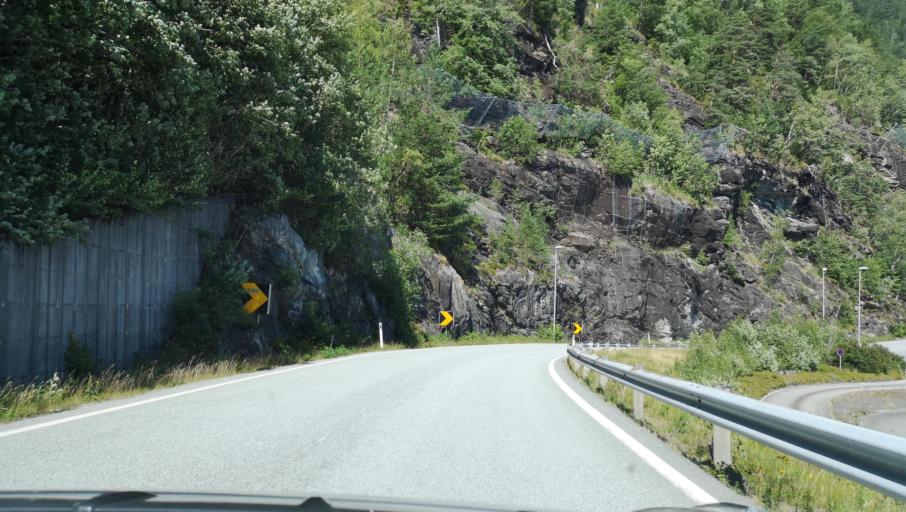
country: NO
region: Hordaland
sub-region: Ulvik
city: Ulvik
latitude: 60.4929
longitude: 6.8921
